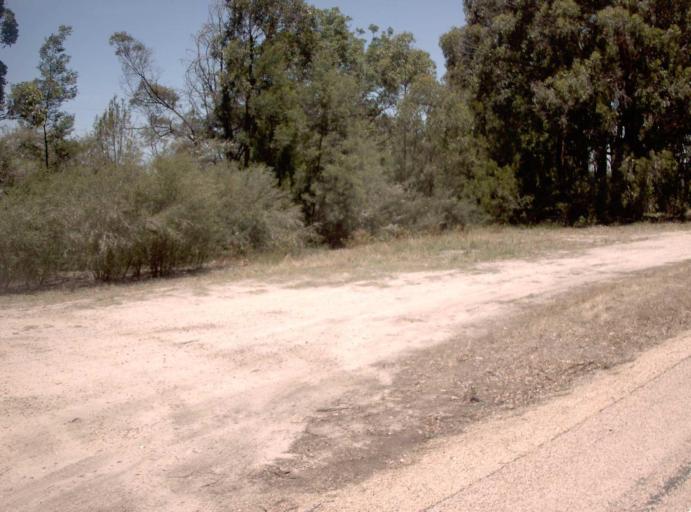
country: AU
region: Victoria
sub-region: East Gippsland
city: Bairnsdale
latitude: -37.7353
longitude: 147.7748
